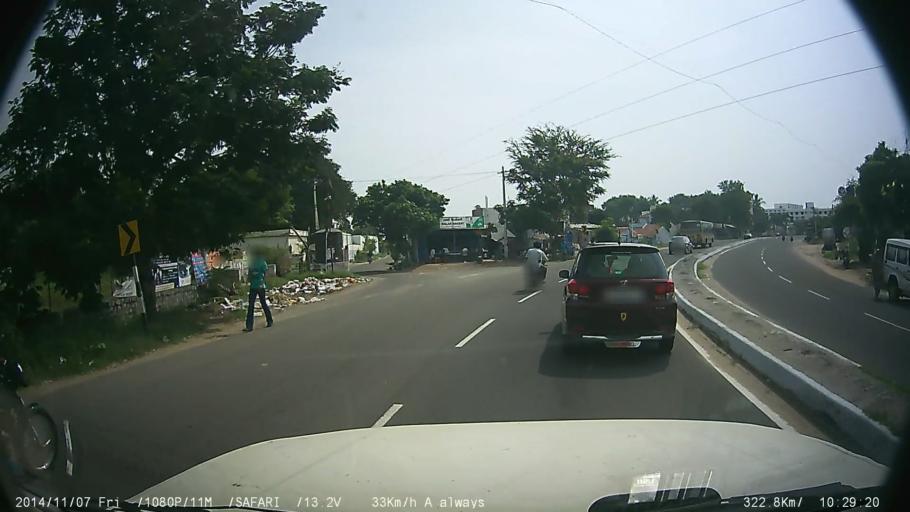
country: IN
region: Tamil Nadu
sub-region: Tiruppur
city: Tiruppur
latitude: 11.1519
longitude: 77.3112
